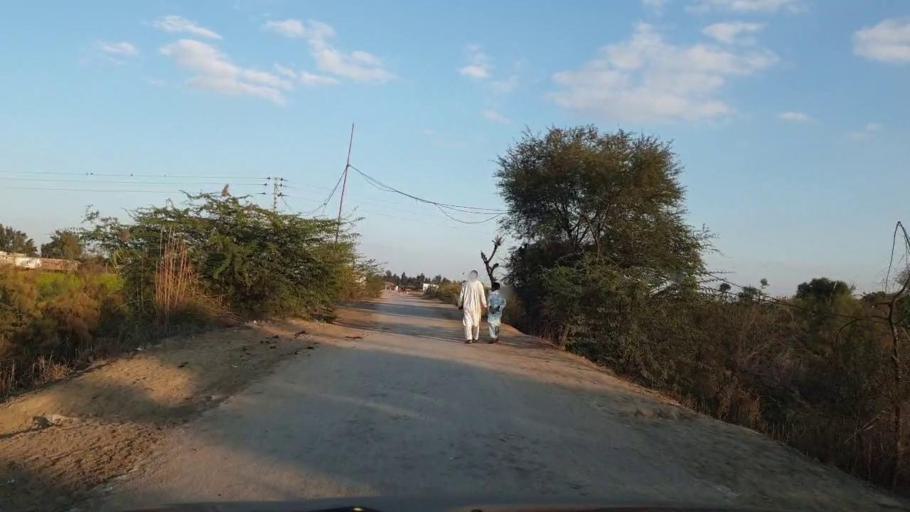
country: PK
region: Sindh
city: Sinjhoro
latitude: 25.9860
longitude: 68.7913
